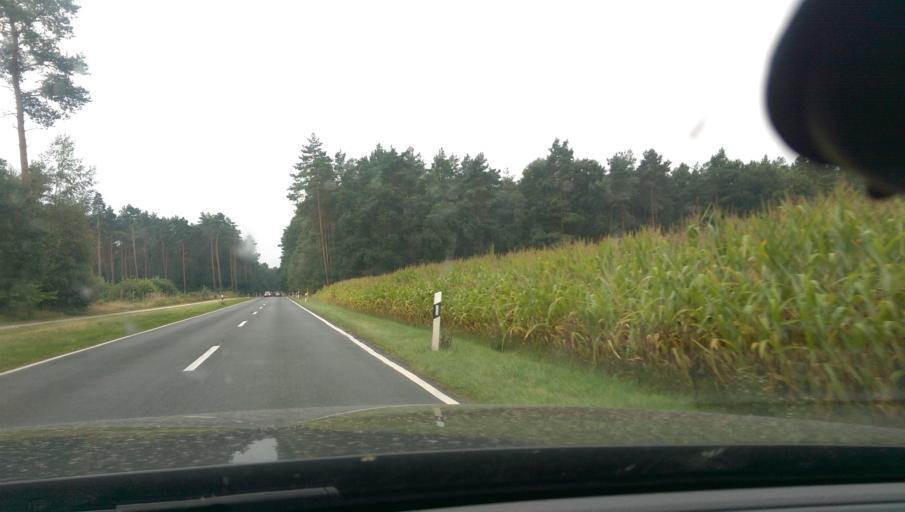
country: DE
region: Lower Saxony
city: Linsburg
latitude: 52.5143
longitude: 9.3244
